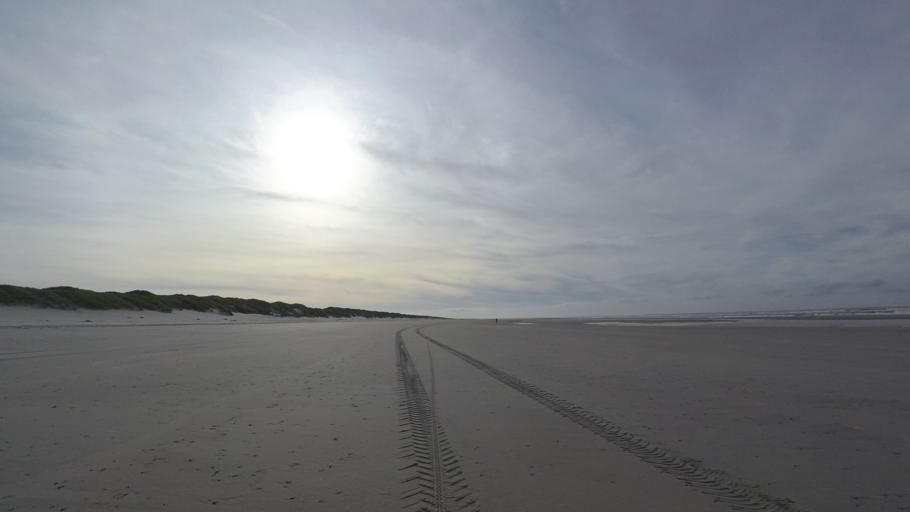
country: NL
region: Friesland
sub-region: Gemeente Ameland
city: Nes
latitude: 53.4656
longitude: 5.8641
